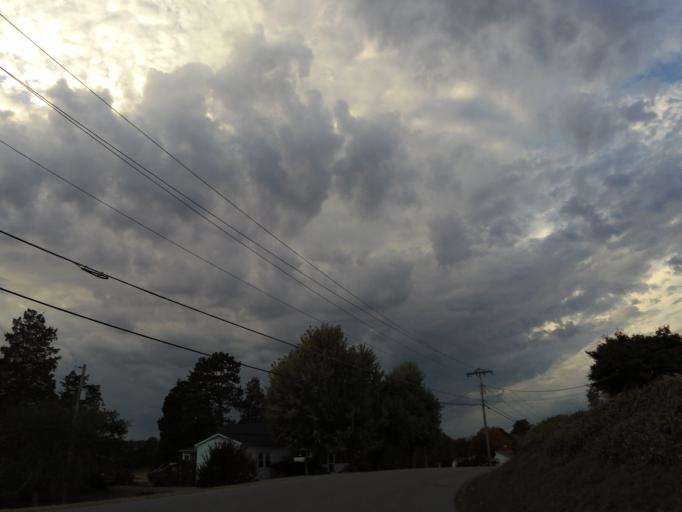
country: US
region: Tennessee
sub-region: Blount County
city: Louisville
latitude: 35.7681
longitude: -84.0459
